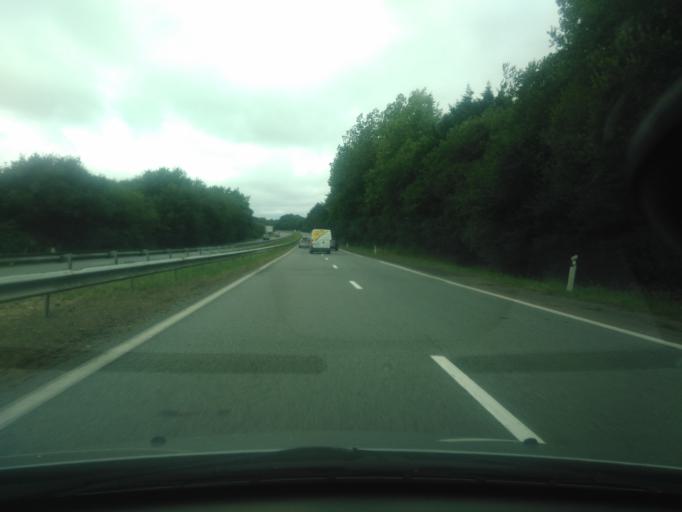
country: FR
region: Brittany
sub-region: Departement des Cotes-d'Armor
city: Trelivan
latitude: 48.4459
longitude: -2.1043
